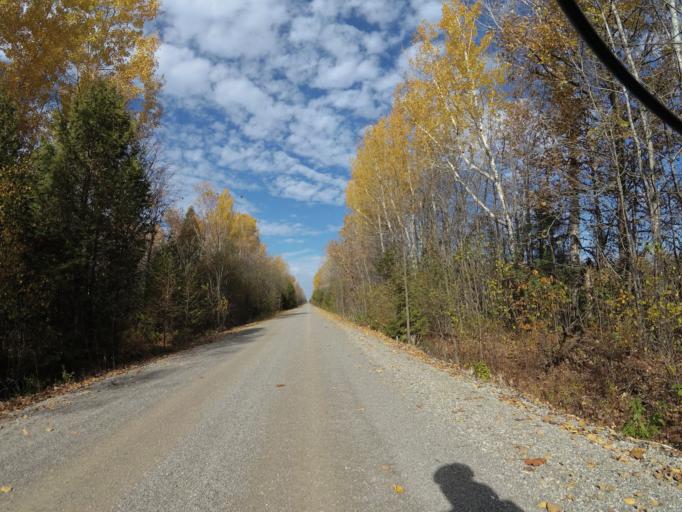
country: CA
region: Ontario
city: Carleton Place
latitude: 45.0316
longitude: -76.0803
